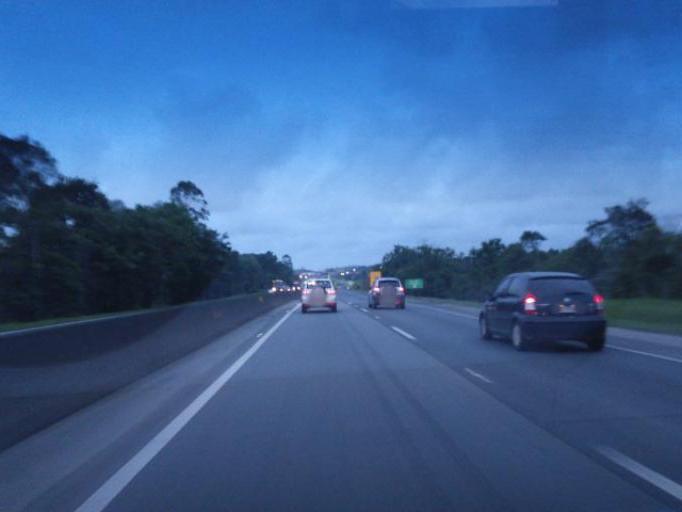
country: BR
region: Santa Catarina
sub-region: Barra Velha
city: Barra Velha
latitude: -26.6142
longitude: -48.7204
